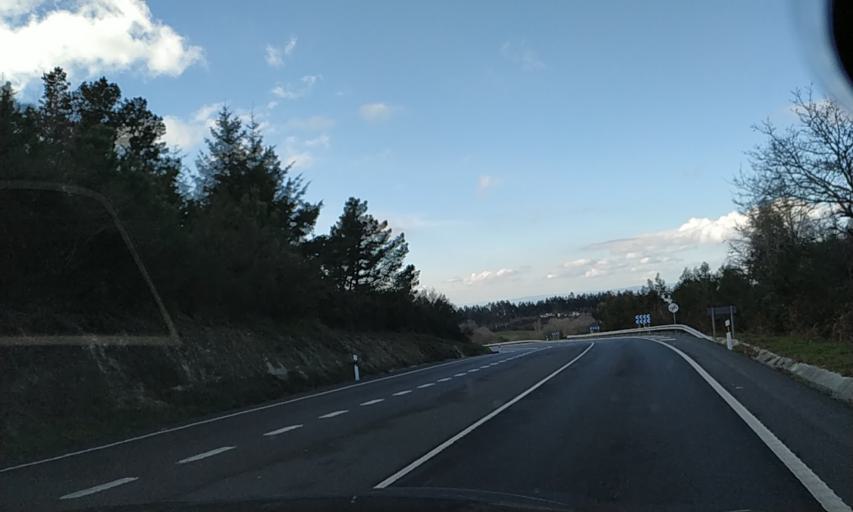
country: ES
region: Galicia
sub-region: Provincia de Pontevedra
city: Silleda
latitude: 42.7079
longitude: -8.3469
